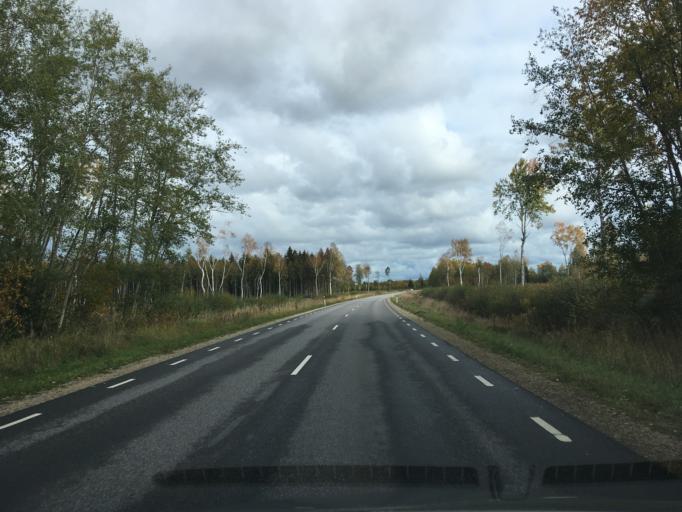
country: EE
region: Harju
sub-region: Anija vald
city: Kehra
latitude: 59.2434
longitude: 25.2986
